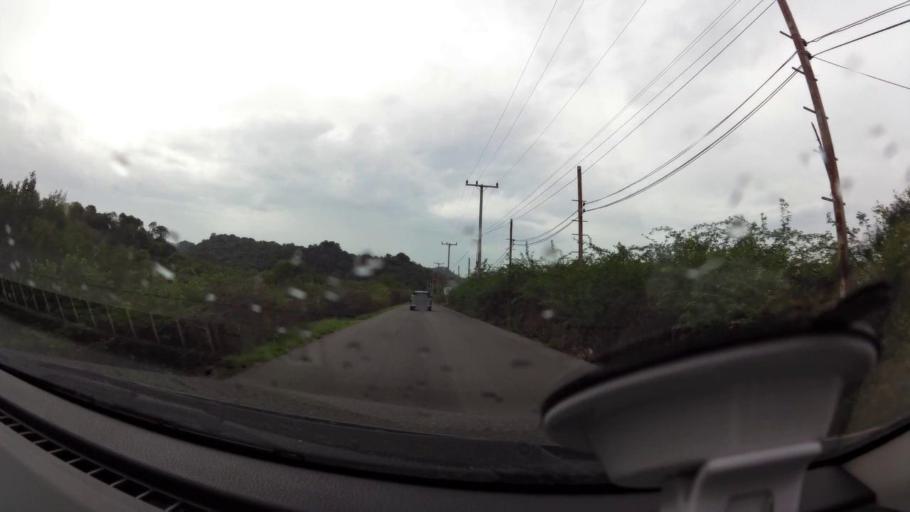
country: TH
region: Prachuap Khiri Khan
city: Pran Buri
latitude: 12.4207
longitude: 99.9800
